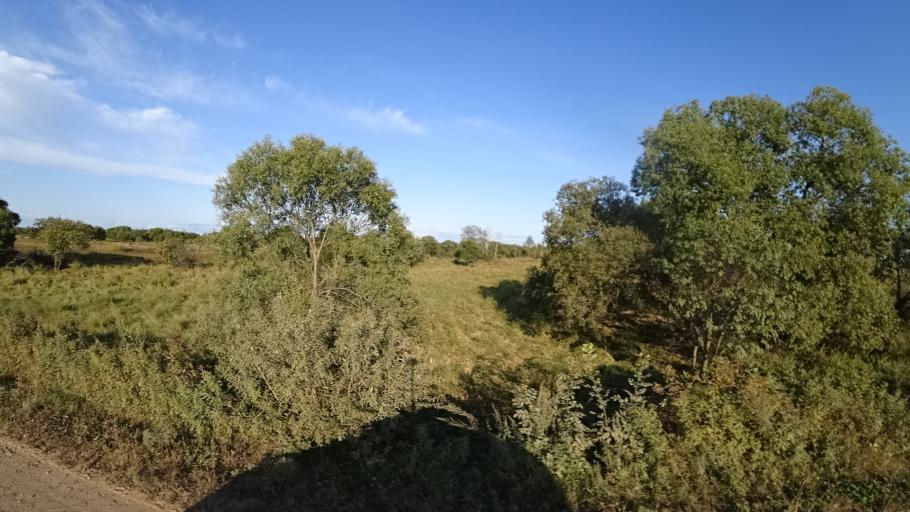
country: RU
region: Amur
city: Arkhara
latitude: 49.3610
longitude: 130.1368
